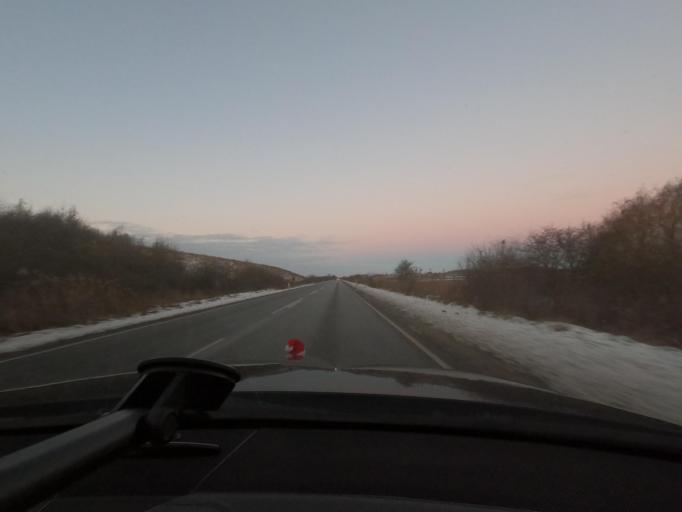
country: DK
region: South Denmark
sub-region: Sonderborg Kommune
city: Sonderborg
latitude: 54.9306
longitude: 9.8360
